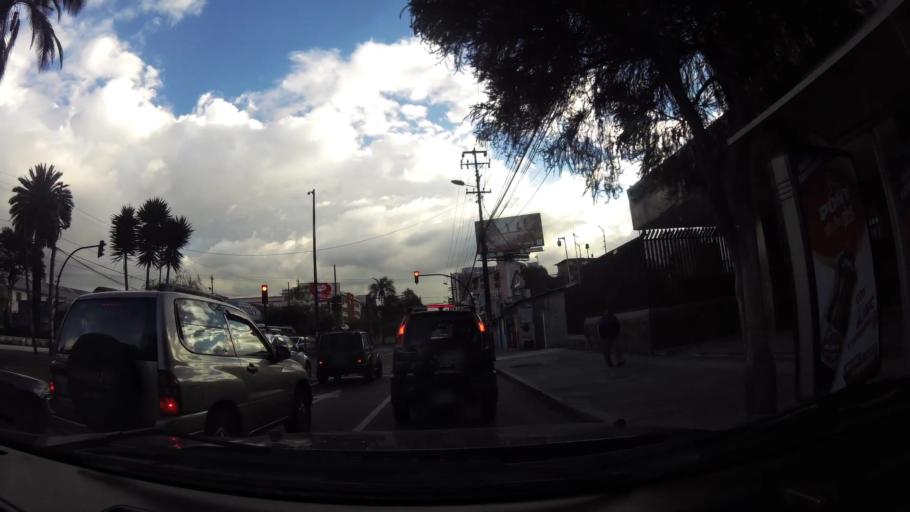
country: EC
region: Pichincha
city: Quito
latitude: -0.2063
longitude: -78.4877
